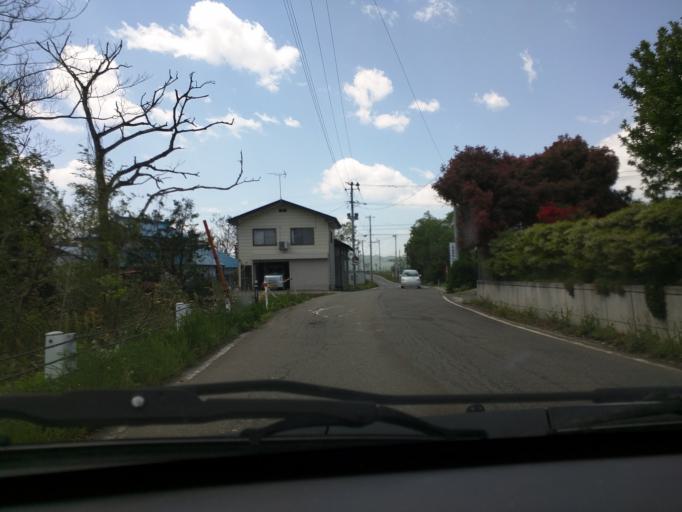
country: JP
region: Fukushima
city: Kitakata
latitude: 37.6407
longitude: 139.7885
